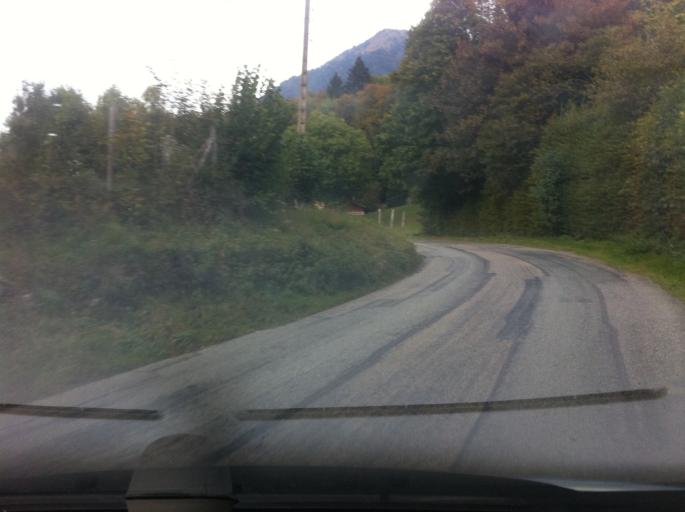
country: FR
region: Rhone-Alpes
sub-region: Departement de la Savoie
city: Mercury
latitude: 45.6702
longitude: 6.3082
